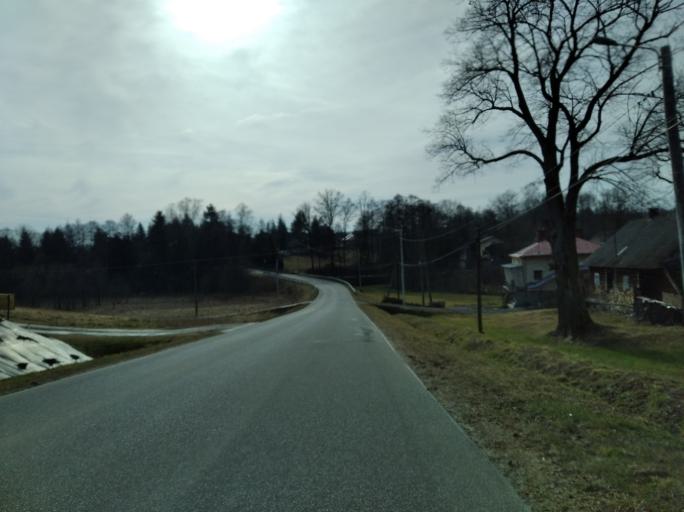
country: PL
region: Subcarpathian Voivodeship
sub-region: Powiat brzozowski
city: Orzechowka
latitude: 49.7400
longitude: 21.9417
